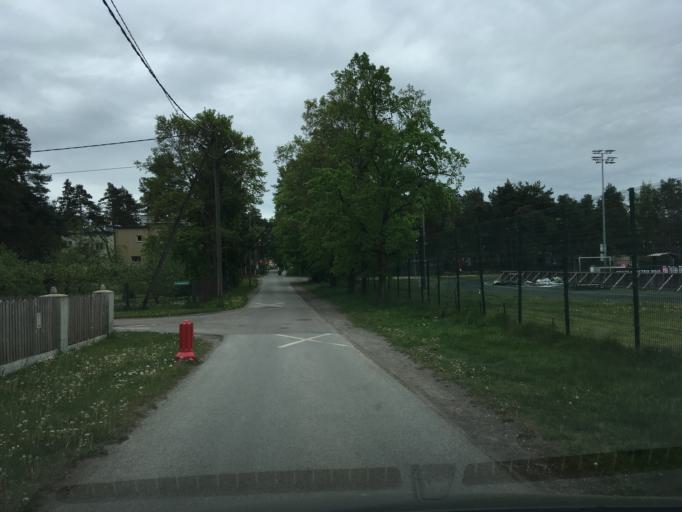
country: EE
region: Harju
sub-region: Saue vald
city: Laagri
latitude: 59.3861
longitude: 24.6609
